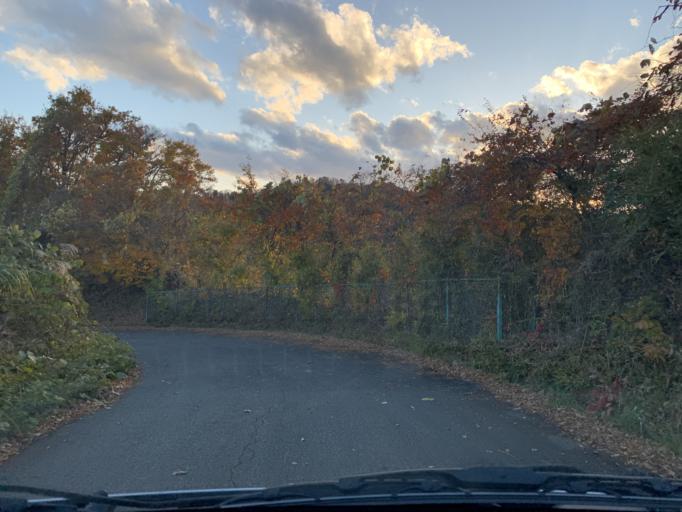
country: JP
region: Iwate
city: Mizusawa
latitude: 39.0449
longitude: 141.0528
